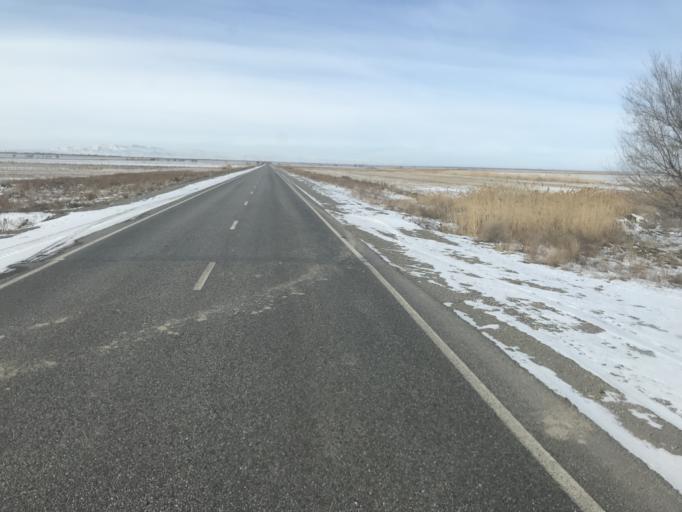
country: KZ
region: Zhambyl
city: Taraz
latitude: 43.0276
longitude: 71.3656
